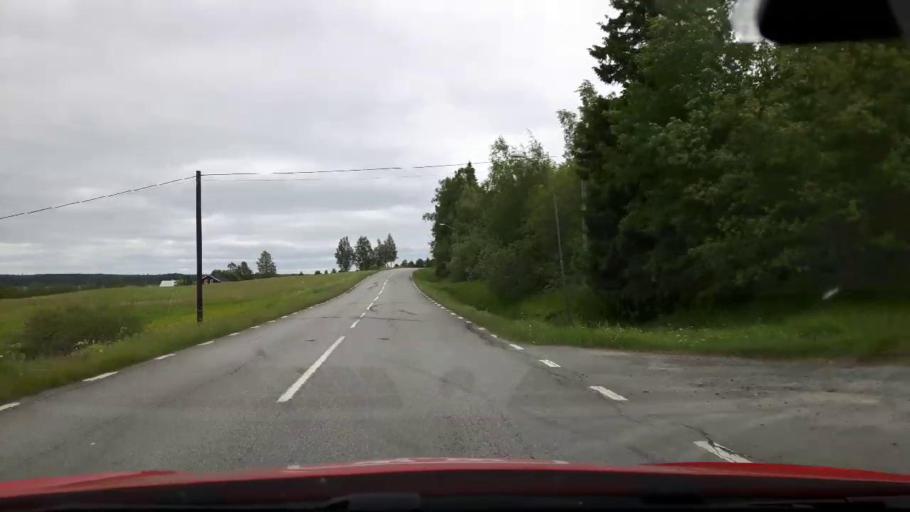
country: SE
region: Jaemtland
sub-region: Stroemsunds Kommun
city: Stroemsund
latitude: 63.5671
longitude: 15.3918
